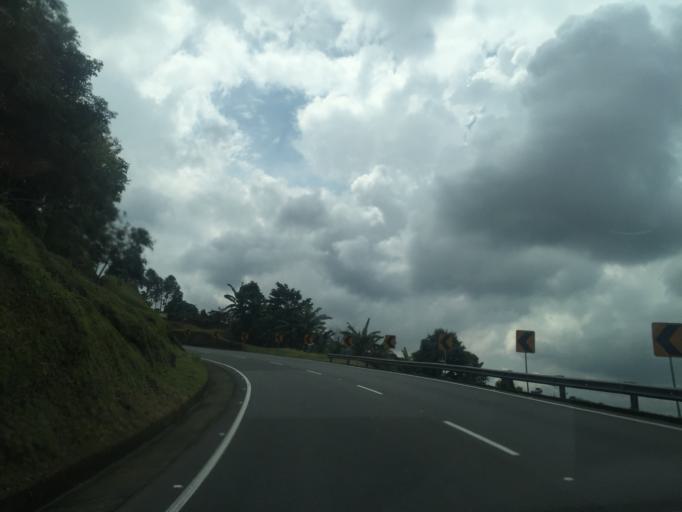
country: CO
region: Risaralda
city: Dos Quebradas
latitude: 4.8531
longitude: -75.6485
